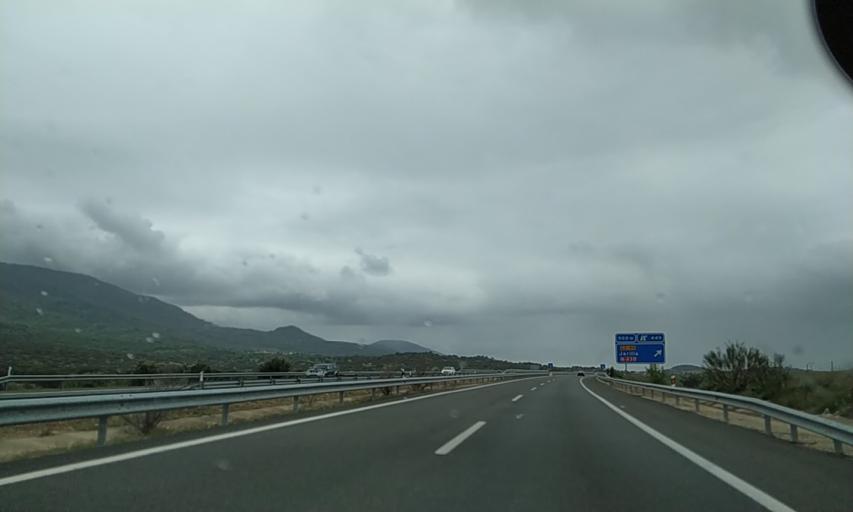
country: ES
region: Extremadura
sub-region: Provincia de Caceres
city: Jarilla
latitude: 40.1967
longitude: -5.9991
